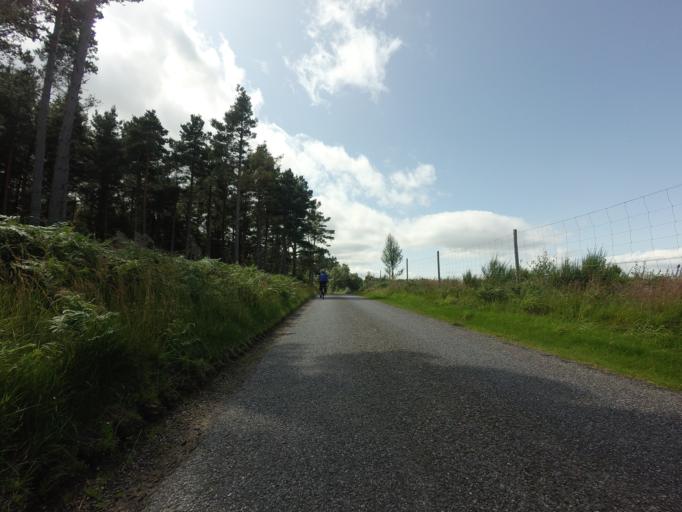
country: GB
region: Scotland
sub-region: Highland
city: Fortrose
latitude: 57.4834
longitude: -4.0336
